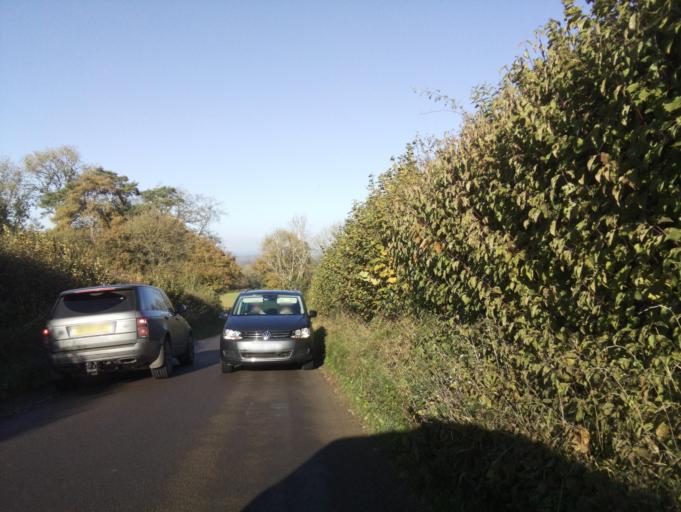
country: GB
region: England
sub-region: Somerset
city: Castle Cary
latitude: 51.0255
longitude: -2.4984
